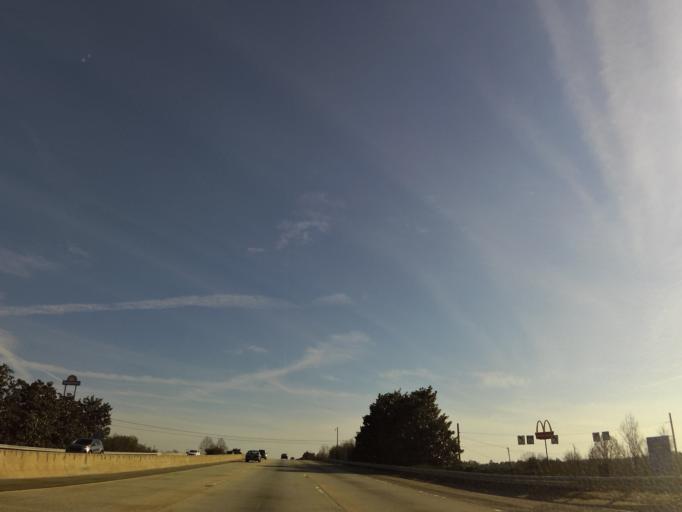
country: US
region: Georgia
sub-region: Muscogee County
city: Columbus
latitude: 32.4843
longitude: -84.9403
